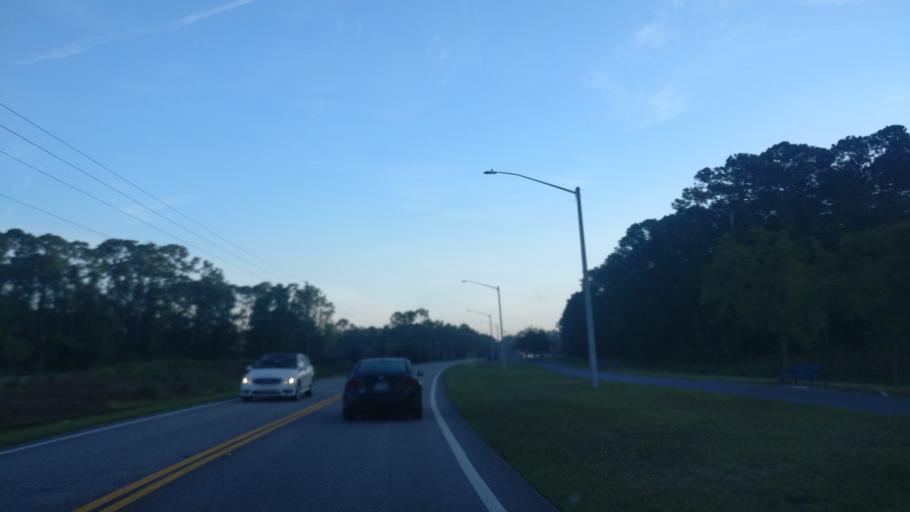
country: US
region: Florida
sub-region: Flagler County
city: Palm Coast
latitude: 29.5417
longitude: -81.2370
